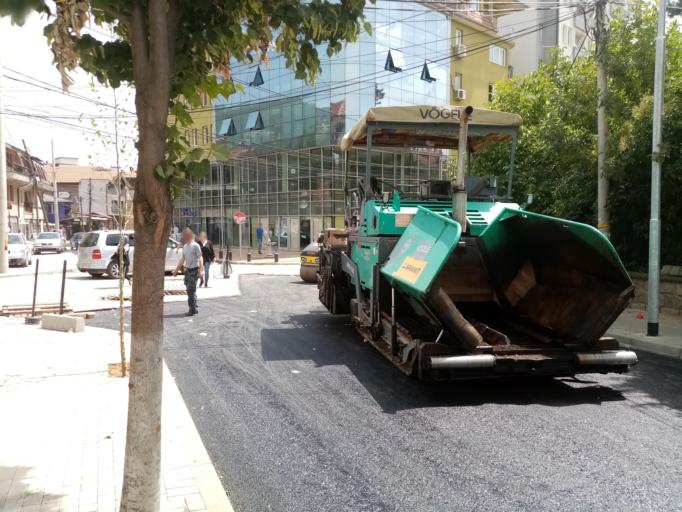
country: MK
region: Tetovo
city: Tetovo
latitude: 42.0061
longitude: 20.9696
